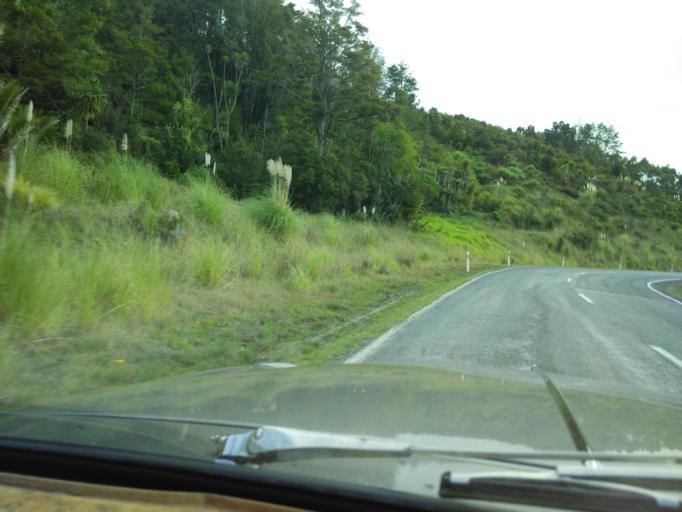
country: NZ
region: Auckland
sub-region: Auckland
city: Wellsford
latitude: -36.3351
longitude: 174.3823
